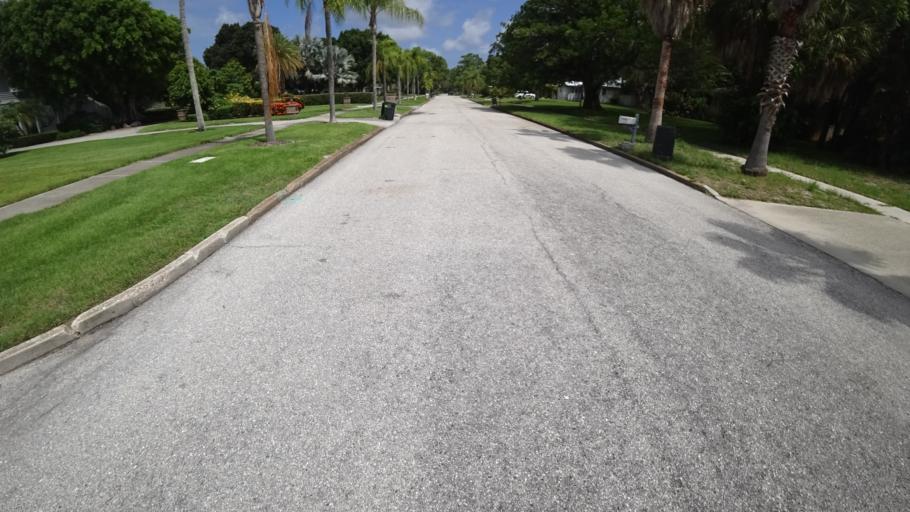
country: US
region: Florida
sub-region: Manatee County
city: Whitfield
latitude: 27.4082
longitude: -82.5748
